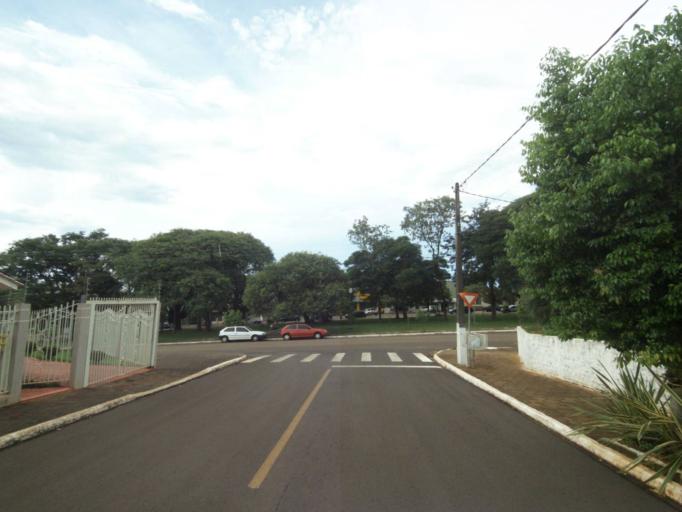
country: BR
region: Parana
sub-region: Guaraniacu
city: Guaraniacu
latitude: -25.1013
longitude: -52.8691
